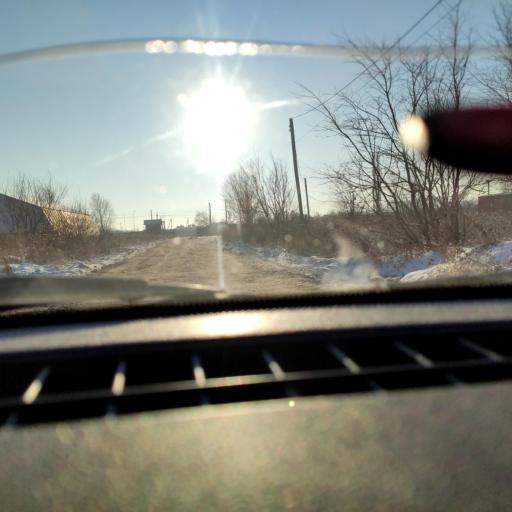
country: RU
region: Bashkortostan
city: Ufa
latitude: 54.6692
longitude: 55.9216
